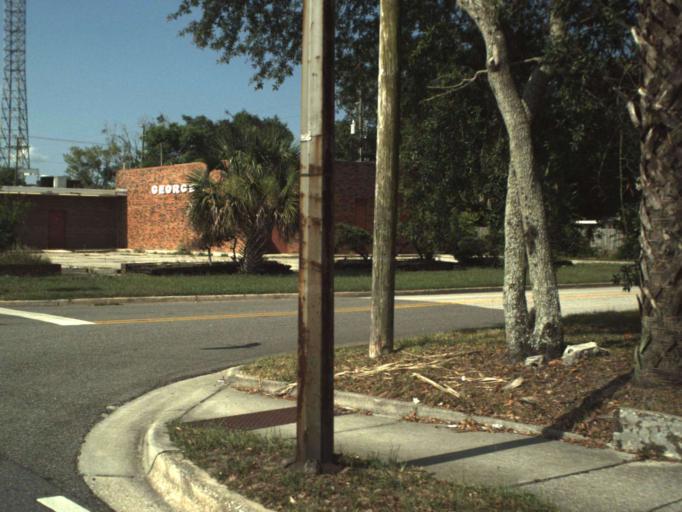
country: US
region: Florida
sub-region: Seminole County
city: Sanford
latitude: 28.8025
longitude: -81.2730
